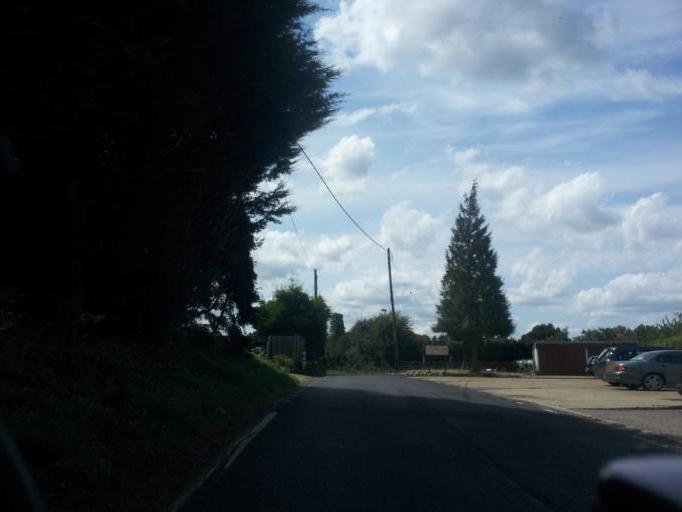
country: GB
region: England
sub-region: Kent
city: Rainham
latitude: 51.3766
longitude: 0.6388
